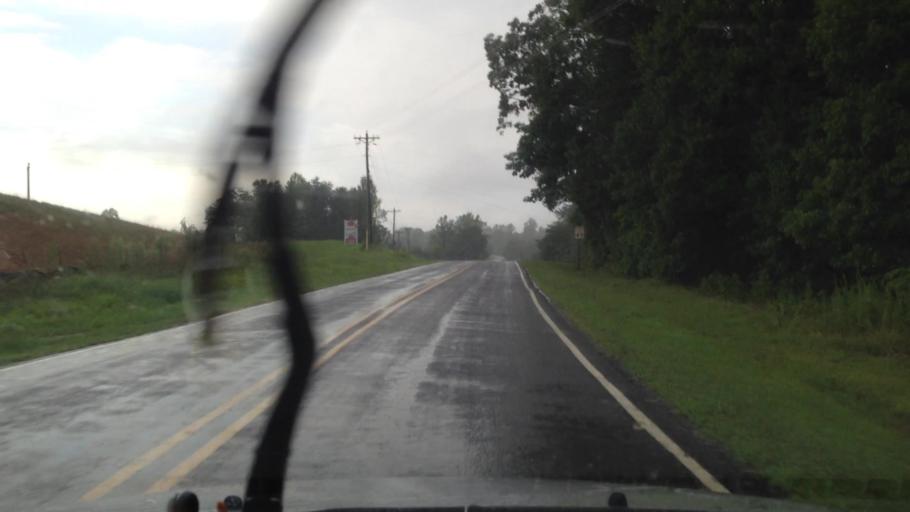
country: US
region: North Carolina
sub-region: Guilford County
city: Oak Ridge
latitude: 36.2116
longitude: -80.0284
